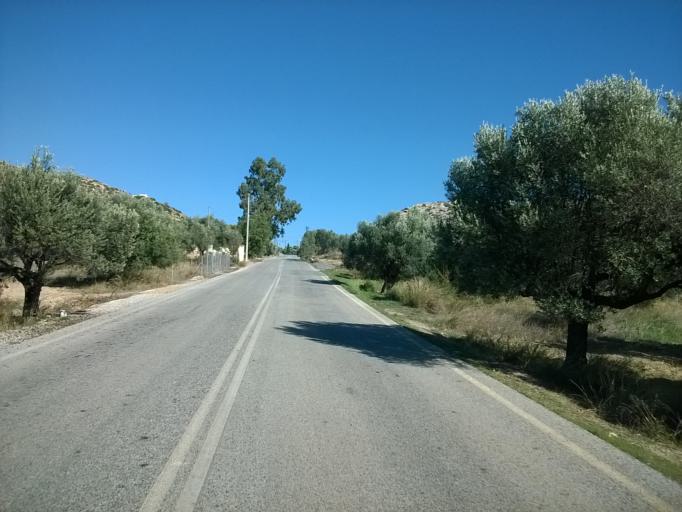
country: GR
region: Attica
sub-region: Nomarchia Anatolikis Attikis
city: Keratea
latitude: 37.7665
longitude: 23.9832
